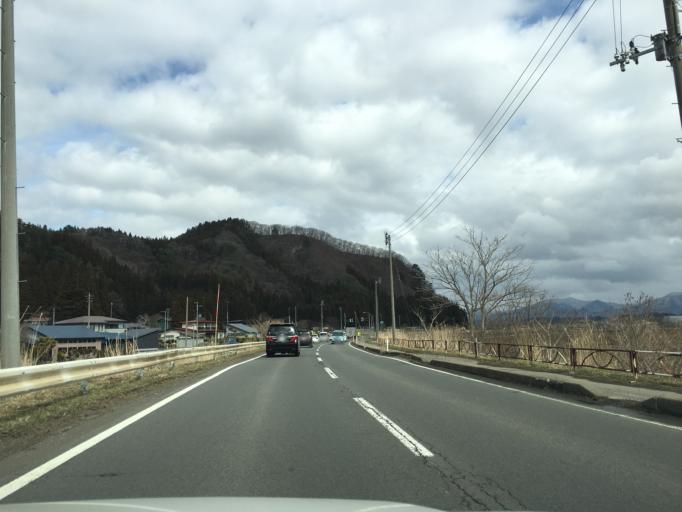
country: JP
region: Akita
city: Hanawa
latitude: 40.2452
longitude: 140.7419
